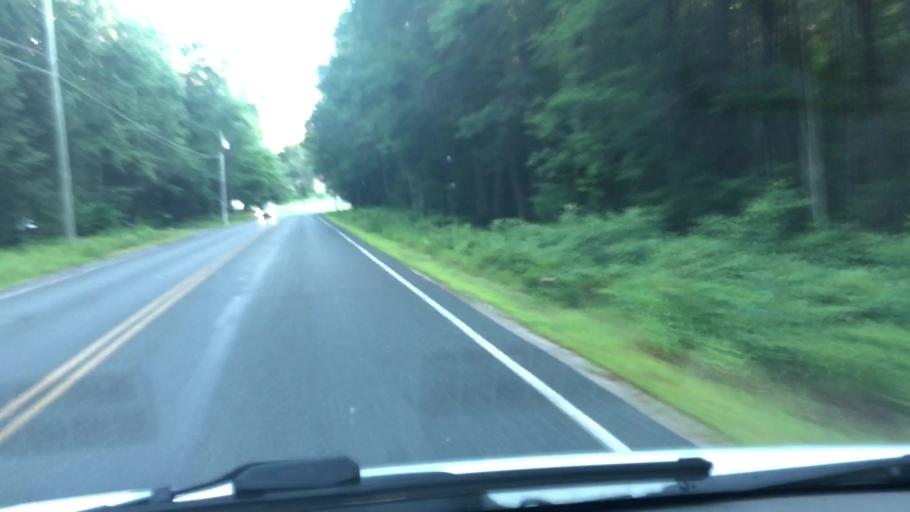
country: US
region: Massachusetts
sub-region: Hampshire County
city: Westhampton
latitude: 42.2713
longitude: -72.7469
